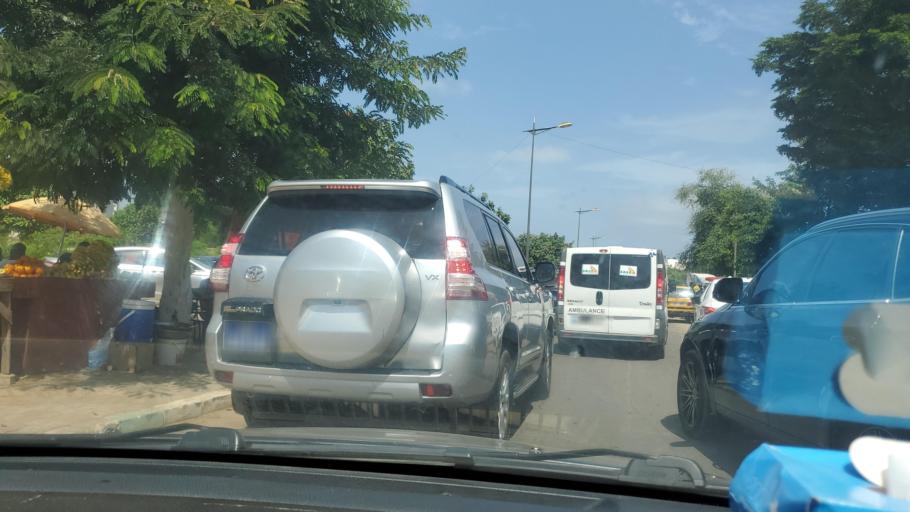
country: SN
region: Dakar
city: Grand Dakar
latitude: 14.7173
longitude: -17.4559
